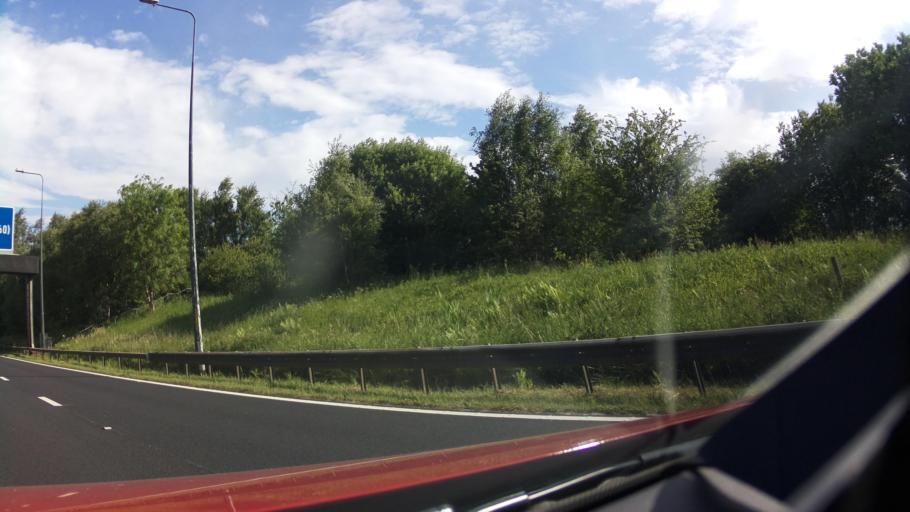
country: GB
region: England
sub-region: Borough of Bolton
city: Kearsley
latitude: 53.5349
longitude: -2.3891
